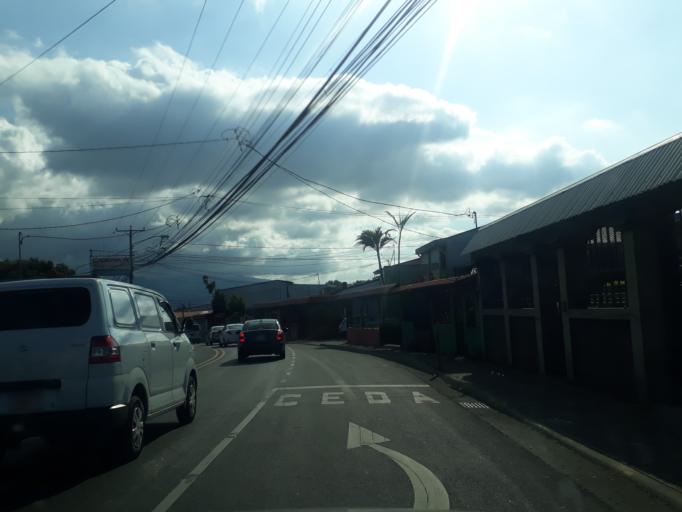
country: CR
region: San Jose
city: San Vicente
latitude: 9.9643
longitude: -84.0408
